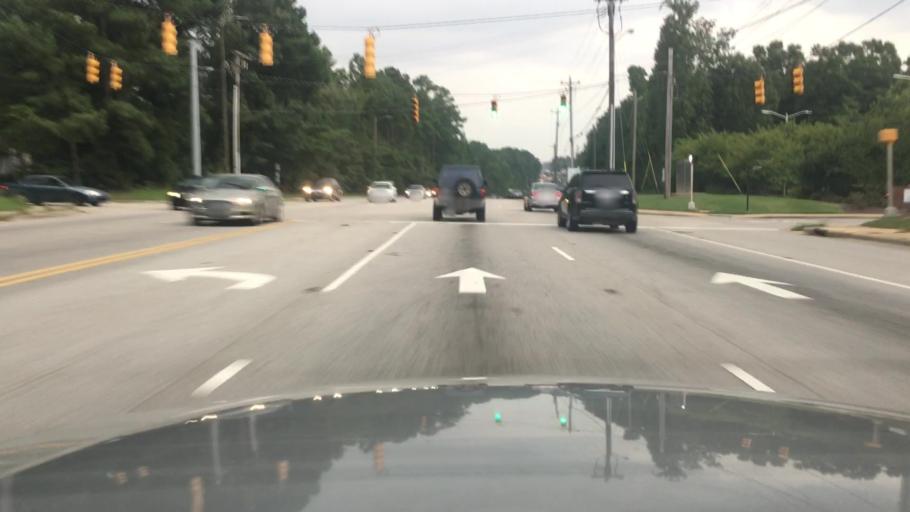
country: US
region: North Carolina
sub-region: Cumberland County
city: Fort Bragg
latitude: 35.0777
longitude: -79.0103
